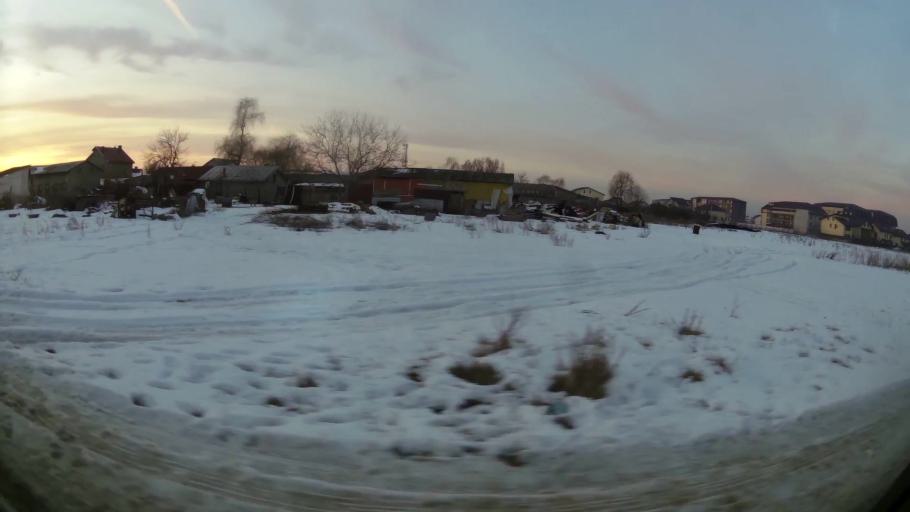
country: RO
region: Ilfov
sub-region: Comuna Magurele
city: Magurele
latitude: 44.3846
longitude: 26.0254
